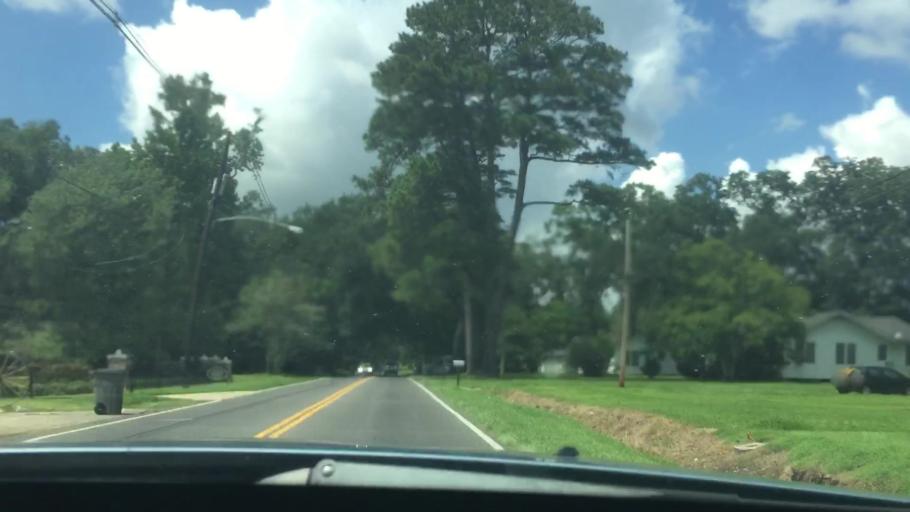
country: US
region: Louisiana
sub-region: East Baton Rouge Parish
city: Gardere
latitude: 30.3799
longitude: -91.1410
